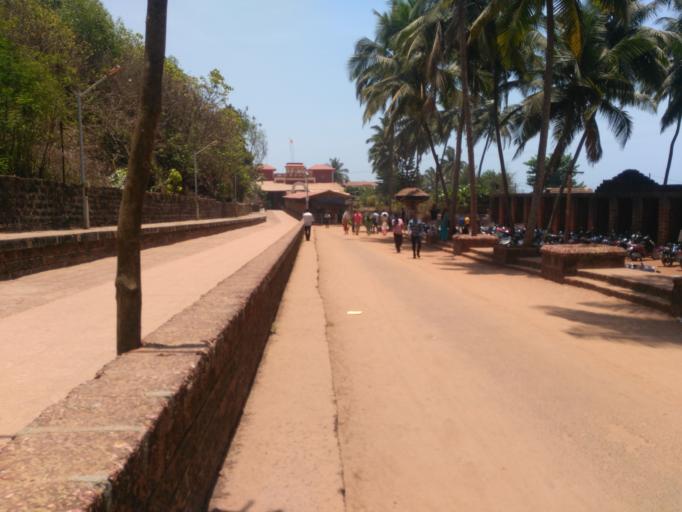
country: IN
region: Maharashtra
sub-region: Ratnagiri
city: Ratnagiri
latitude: 17.1465
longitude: 73.2665
